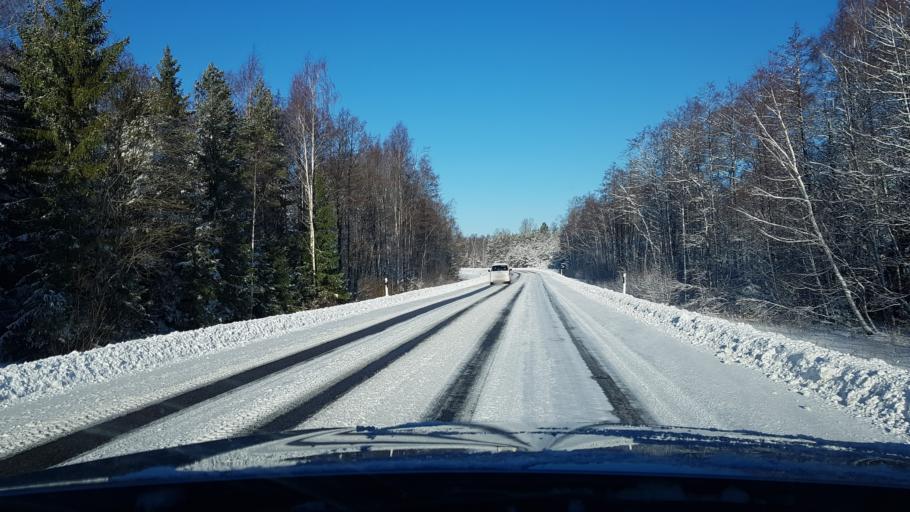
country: EE
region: Hiiumaa
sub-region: Kaerdla linn
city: Kardla
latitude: 58.9638
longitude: 22.7722
